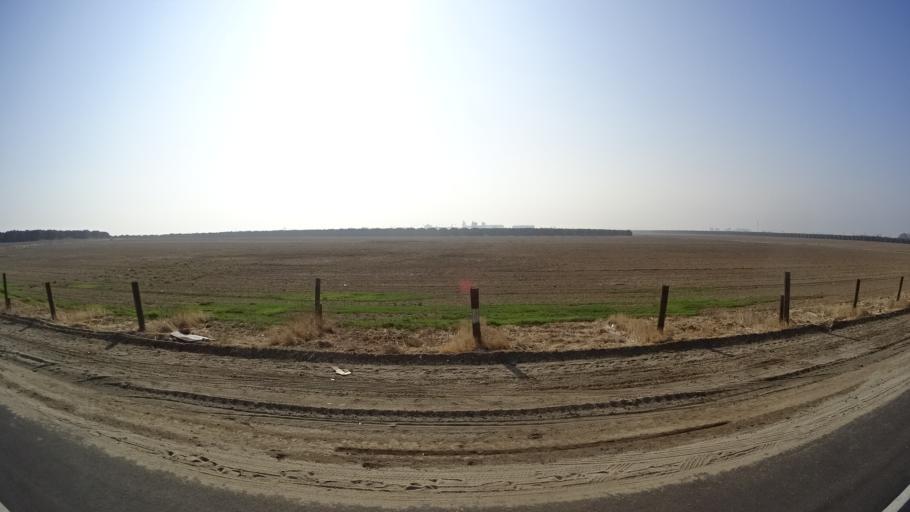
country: US
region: California
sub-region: Kern County
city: Lamont
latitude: 35.3618
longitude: -118.8845
